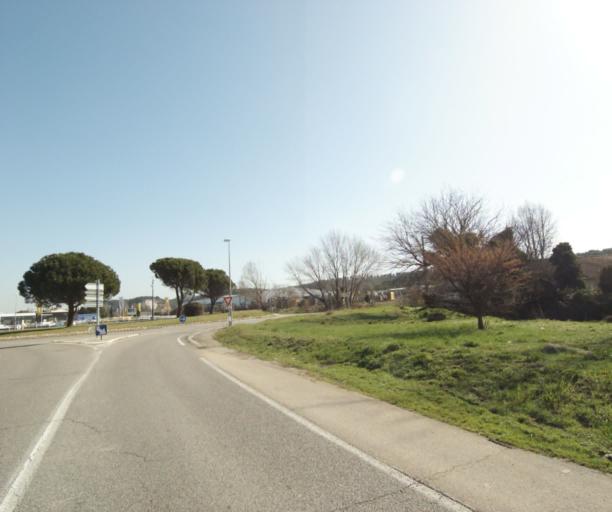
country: FR
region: Provence-Alpes-Cote d'Azur
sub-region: Departement des Bouches-du-Rhone
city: Cabries
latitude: 43.4259
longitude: 5.3866
